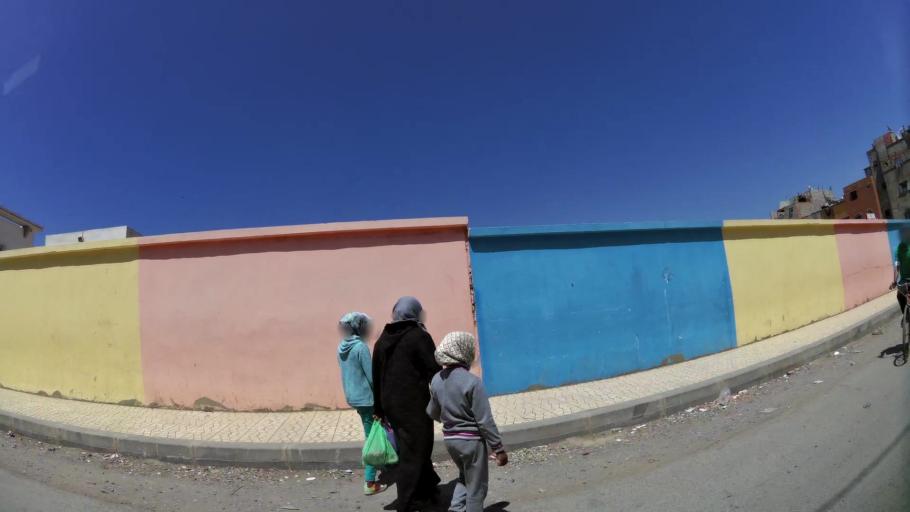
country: MA
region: Rabat-Sale-Zemmour-Zaer
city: Sale
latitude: 34.0637
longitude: -6.7795
